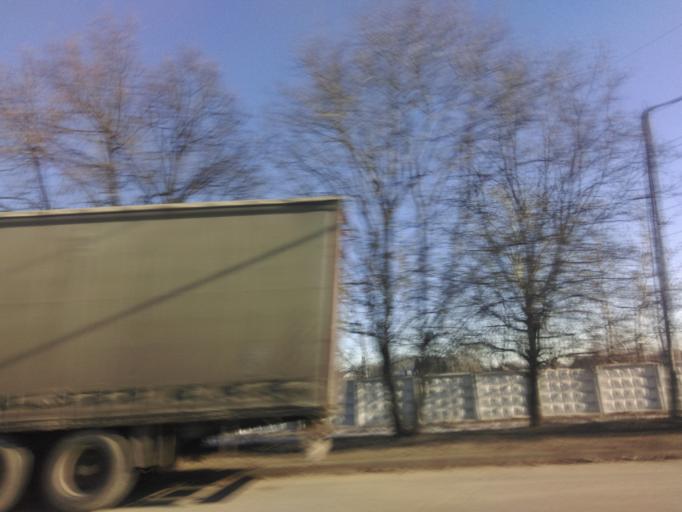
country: RU
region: Moskovskaya
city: Odintsovo
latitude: 55.6709
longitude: 37.3057
